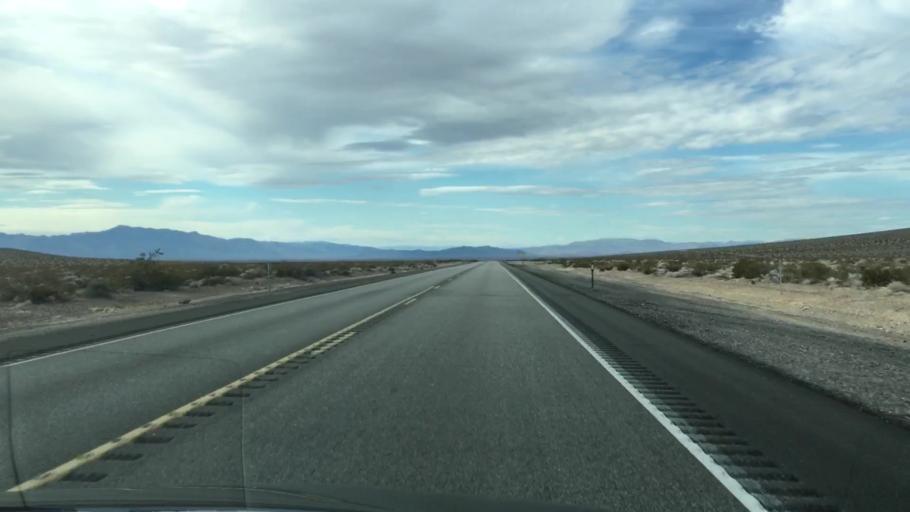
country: US
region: Nevada
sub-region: Nye County
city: Beatty
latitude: 36.6317
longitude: -116.3264
